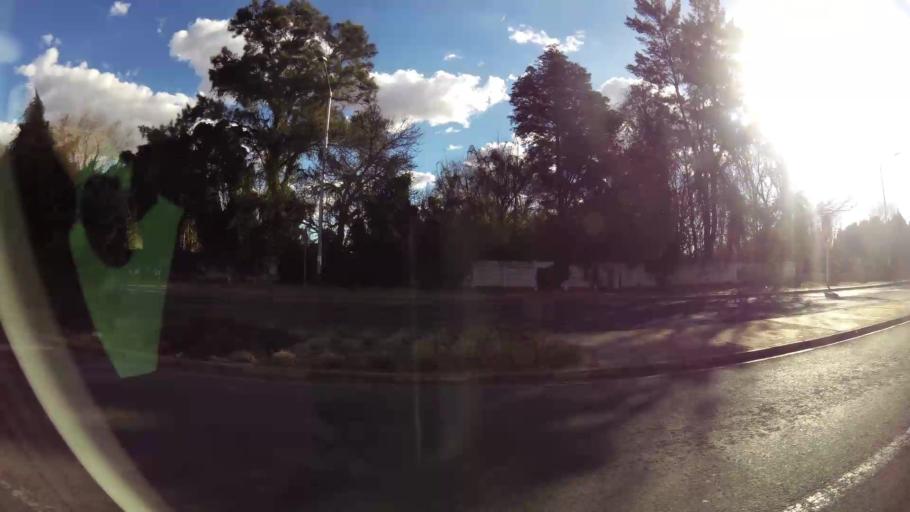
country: ZA
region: North-West
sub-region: Dr Kenneth Kaunda District Municipality
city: Klerksdorp
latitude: -26.8514
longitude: 26.6641
